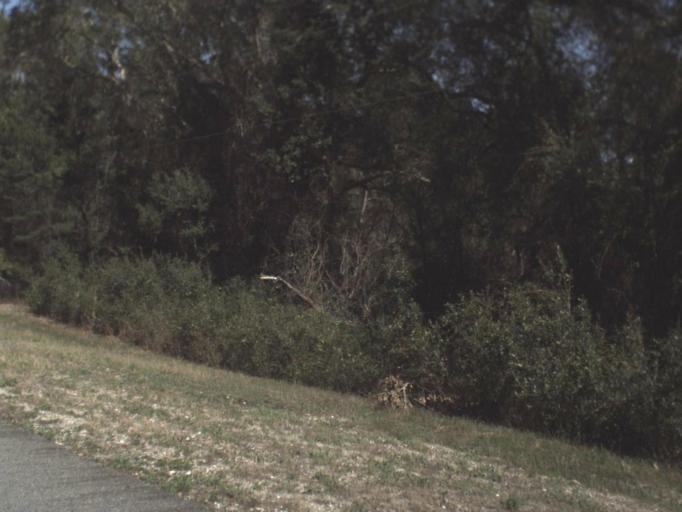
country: US
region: Florida
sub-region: Wakulla County
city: Crawfordville
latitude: 29.9271
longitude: -84.4004
